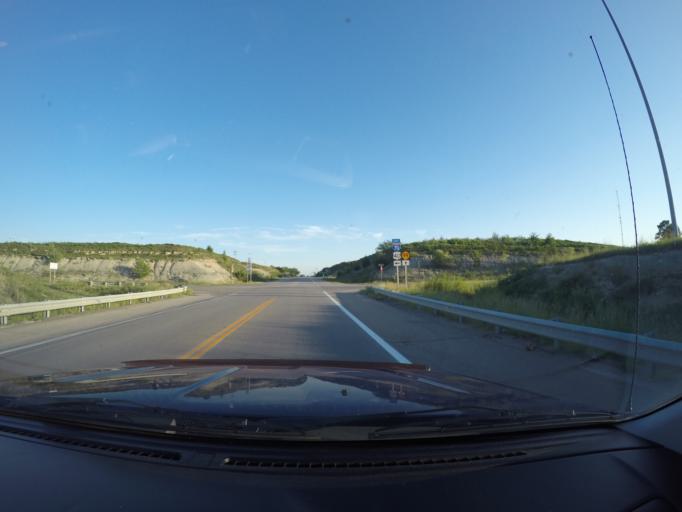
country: US
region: Kansas
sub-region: Wabaunsee County
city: Alma
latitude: 39.0655
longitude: -96.2891
